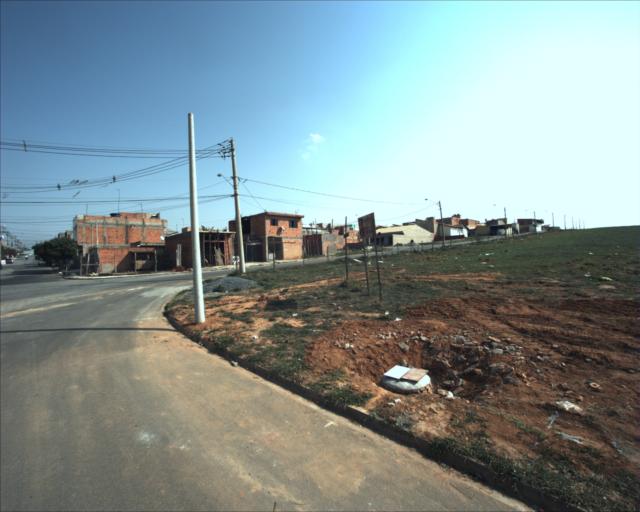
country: BR
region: Sao Paulo
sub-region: Sorocaba
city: Sorocaba
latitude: -23.4215
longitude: -47.4661
